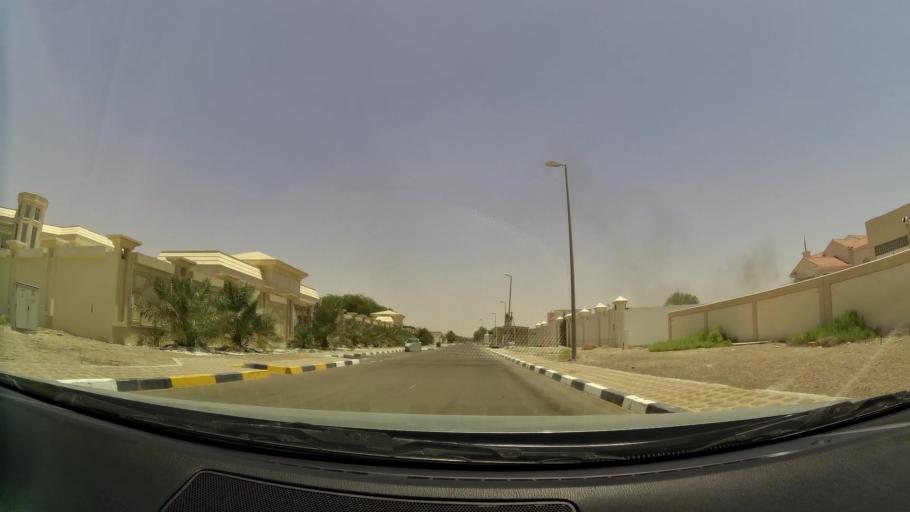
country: OM
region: Al Buraimi
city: Al Buraymi
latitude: 24.2829
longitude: 55.7403
